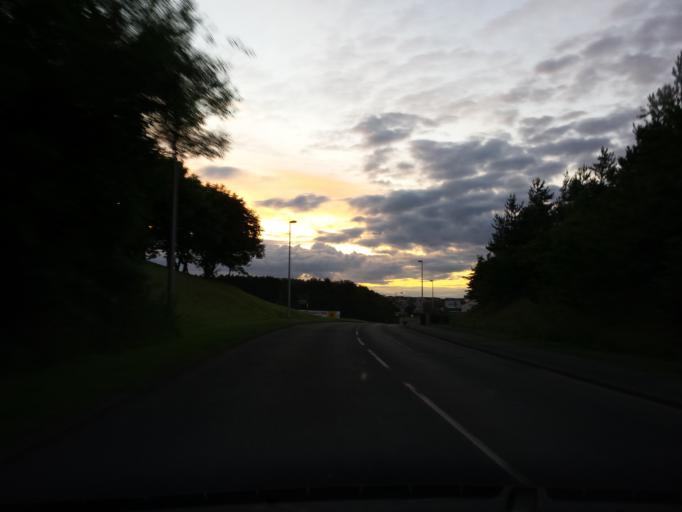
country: GB
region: Scotland
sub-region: The Scottish Borders
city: Eyemouth
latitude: 55.8689
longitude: -2.0994
